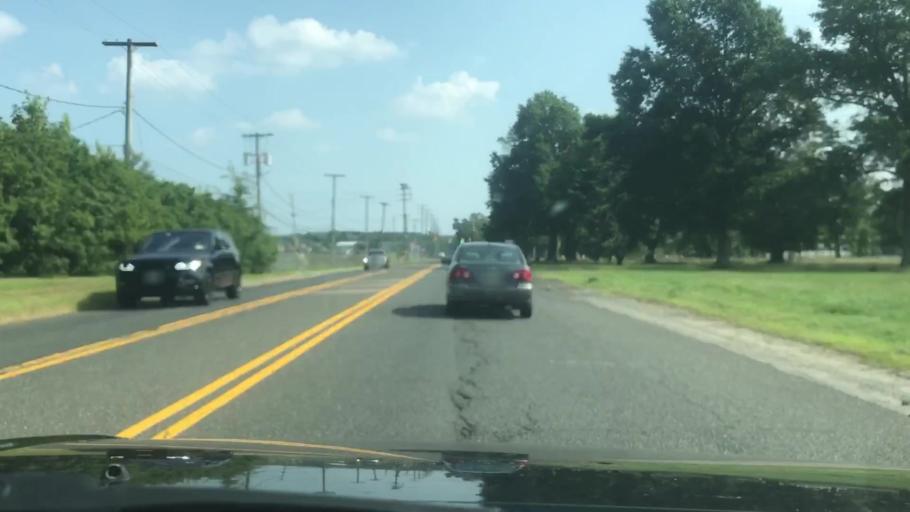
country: US
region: New Jersey
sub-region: Monmouth County
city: Oceanport
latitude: 40.3198
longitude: -74.0352
